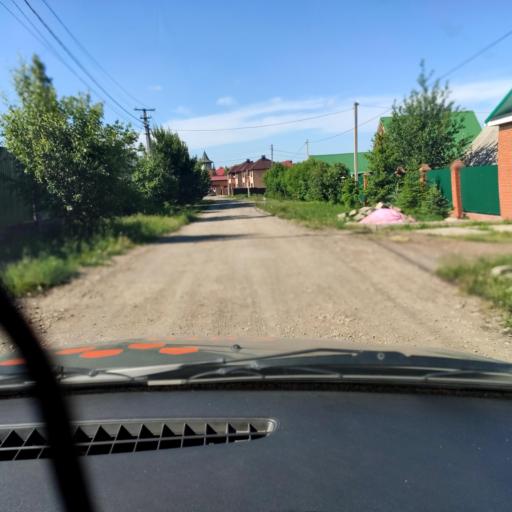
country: RU
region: Bashkortostan
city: Ufa
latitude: 54.6109
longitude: 55.9164
